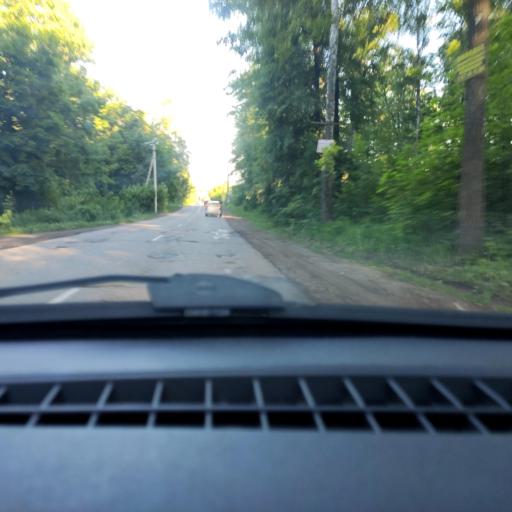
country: RU
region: Bashkortostan
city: Avdon
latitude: 54.6475
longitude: 55.7023
